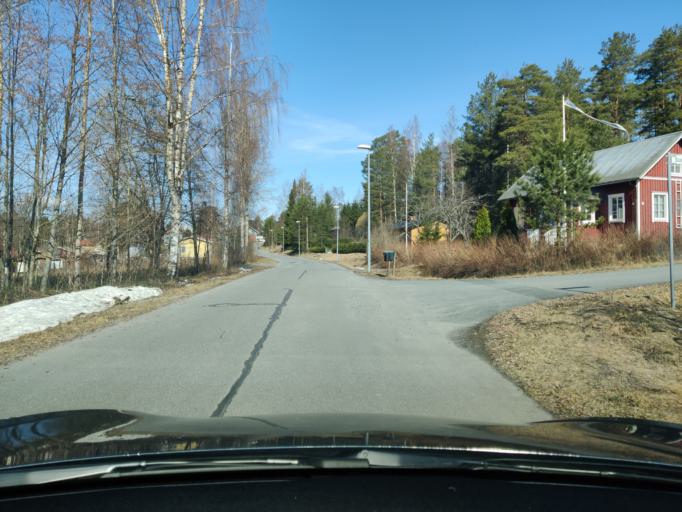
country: FI
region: Northern Savo
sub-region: Kuopio
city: Vehmersalmi
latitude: 62.7589
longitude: 28.0309
